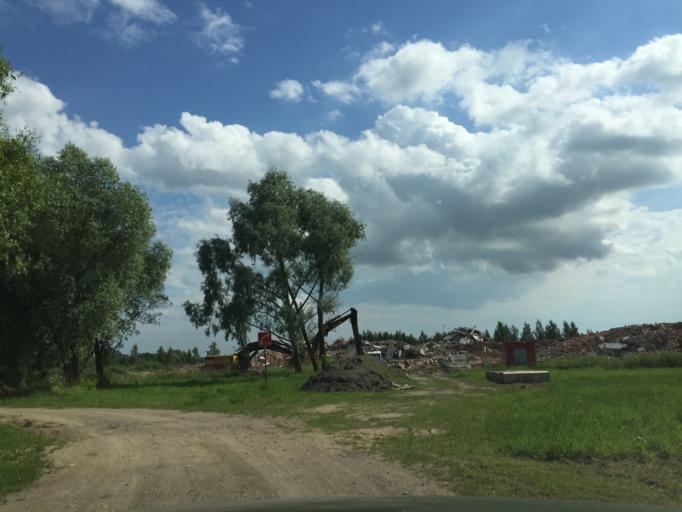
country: LV
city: Tervete
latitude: 56.6185
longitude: 23.4407
